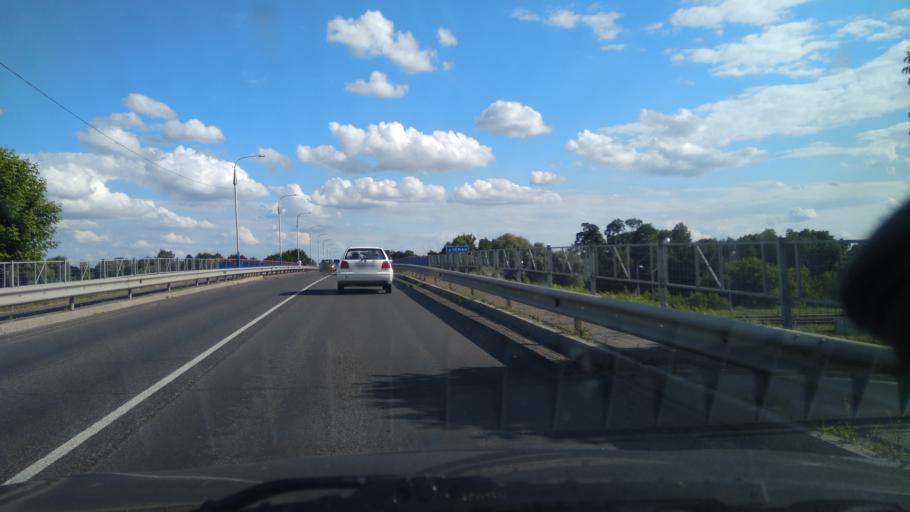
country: BY
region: Grodnenskaya
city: Masty
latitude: 53.4049
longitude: 24.5360
